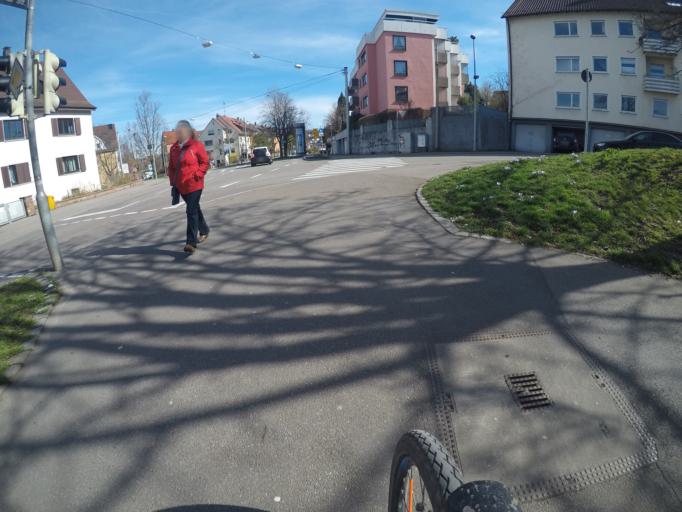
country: DE
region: Baden-Wuerttemberg
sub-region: Regierungsbezirk Stuttgart
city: Stuttgart Feuerbach
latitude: 48.8096
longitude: 9.1521
